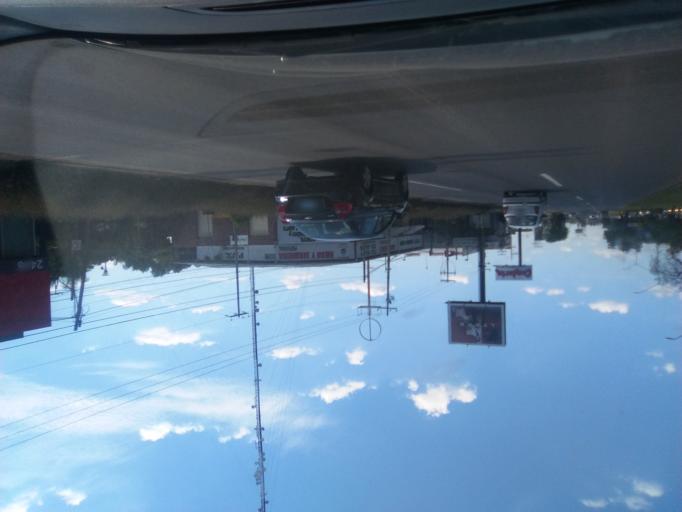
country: MX
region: Guanajuato
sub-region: Leon
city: Ladrilleras del Refugio
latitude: 21.0673
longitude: -101.5923
